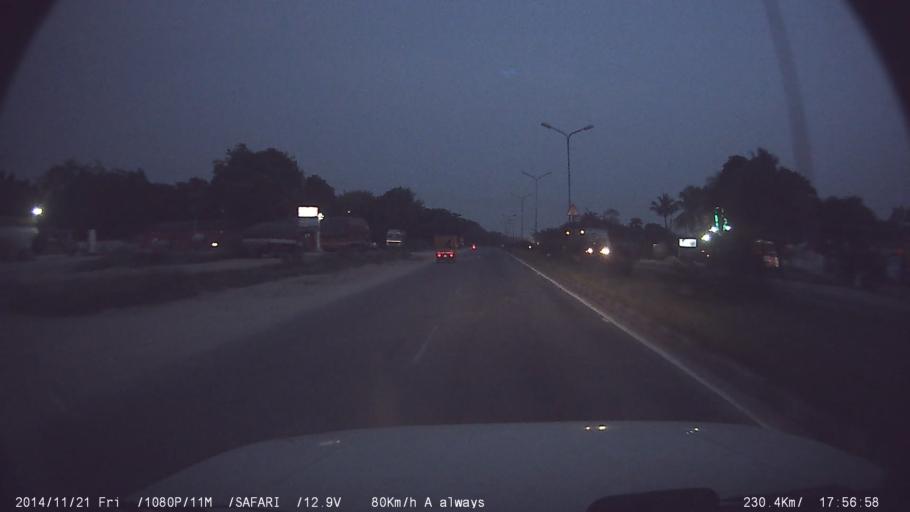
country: IN
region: Tamil Nadu
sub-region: Vellore
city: Walajapet
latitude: 12.9084
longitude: 79.4077
